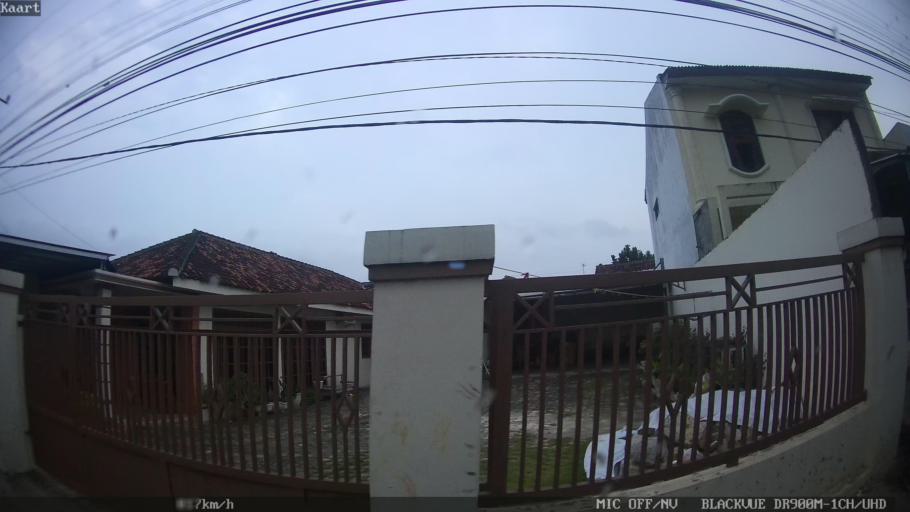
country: ID
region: Lampung
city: Kedaton
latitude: -5.3993
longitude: 105.2705
